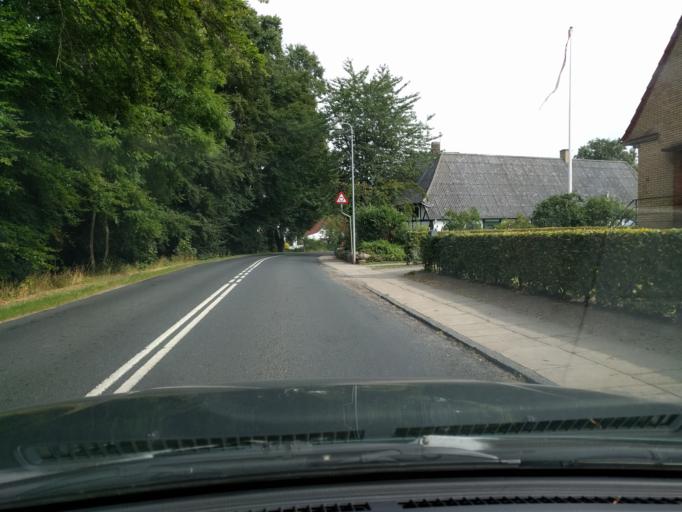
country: DK
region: South Denmark
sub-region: Odense Kommune
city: Bullerup
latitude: 55.3983
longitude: 10.4612
